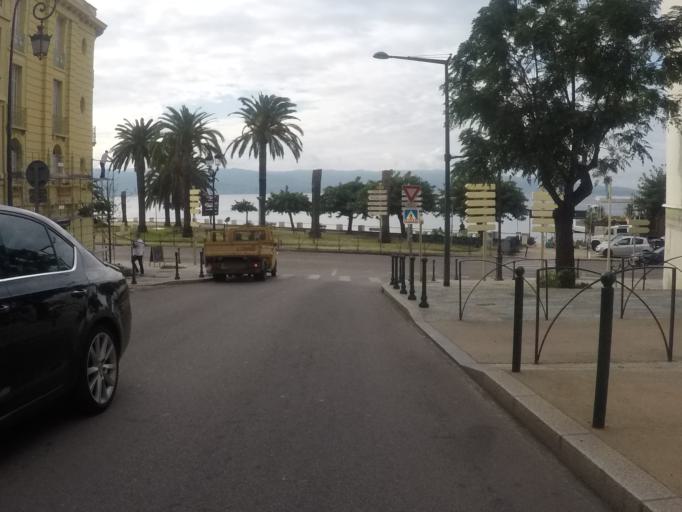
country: FR
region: Corsica
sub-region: Departement de la Corse-du-Sud
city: Ajaccio
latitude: 41.9134
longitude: 8.7256
